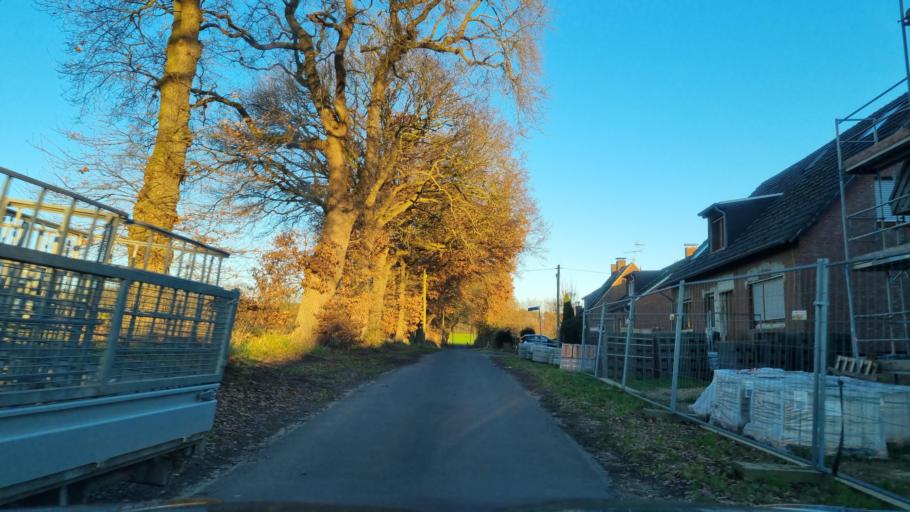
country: DE
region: North Rhine-Westphalia
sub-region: Regierungsbezirk Dusseldorf
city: Kranenburg
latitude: 51.7717
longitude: 6.0530
